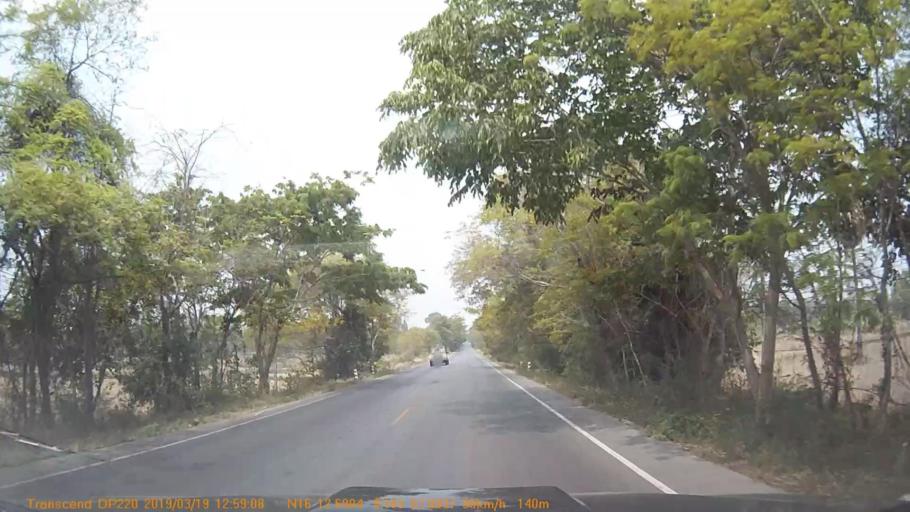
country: TH
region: Roi Et
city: Waeng
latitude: 16.2117
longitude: 103.9514
